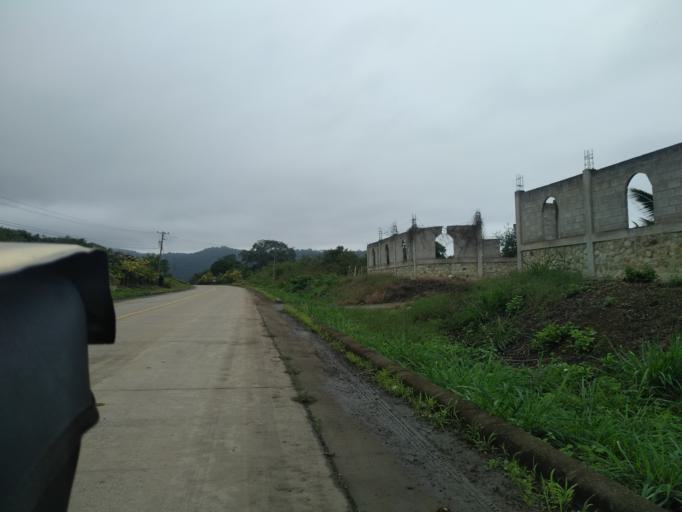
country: EC
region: Manabi
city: Jipijapa
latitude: -1.6630
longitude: -80.8148
